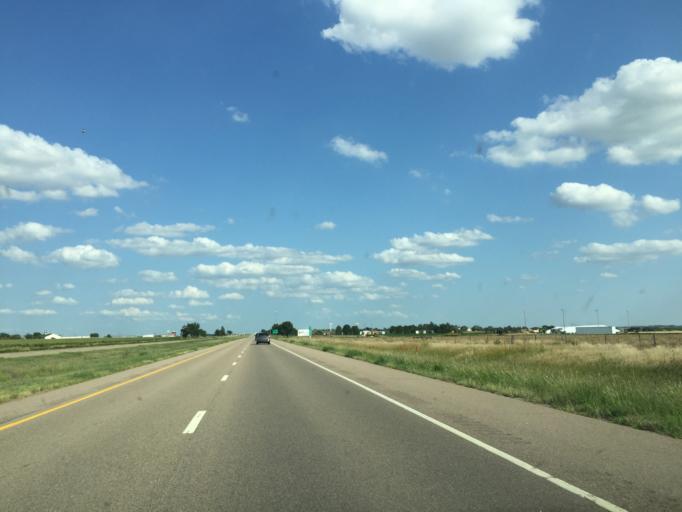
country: US
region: Kansas
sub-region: Gove County
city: Gove
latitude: 39.0622
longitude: -100.2510
